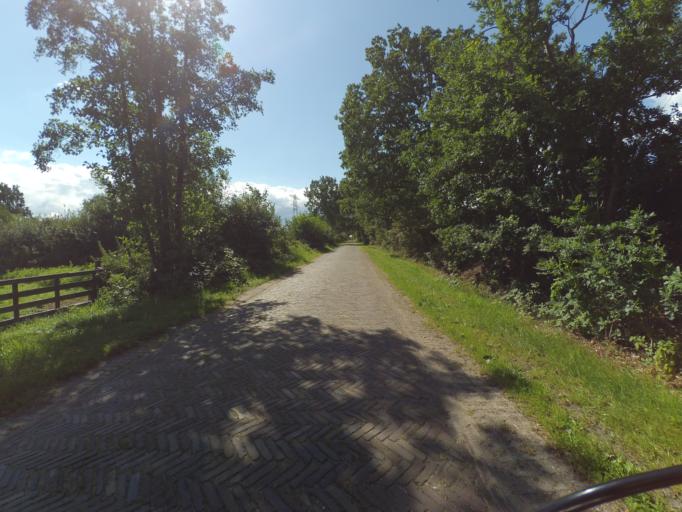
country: NL
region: Friesland
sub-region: Gemeente Achtkarspelen
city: Twijzelerheide
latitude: 53.2217
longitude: 6.0435
